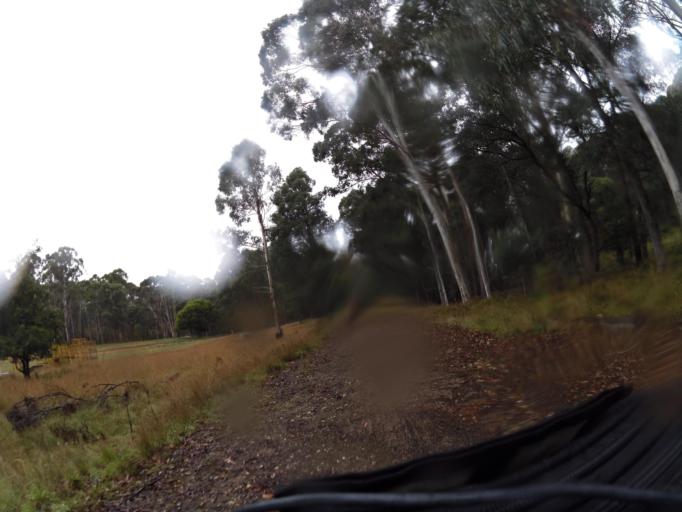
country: AU
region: New South Wales
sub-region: Greater Hume Shire
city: Holbrook
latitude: -36.1627
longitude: 147.4861
